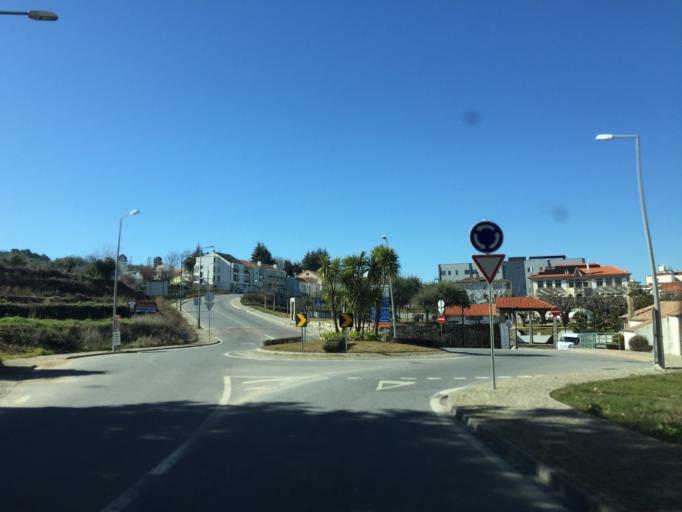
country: PT
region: Castelo Branco
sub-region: Concelho do Fundao
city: Fundao
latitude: 40.1340
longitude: -7.4982
